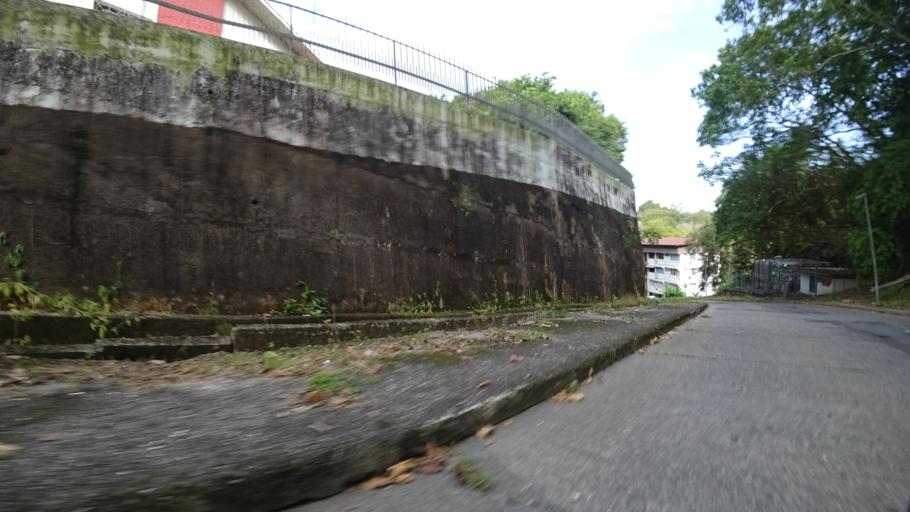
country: BN
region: Brunei and Muara
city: Bandar Seri Begawan
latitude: 4.8845
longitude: 114.9240
